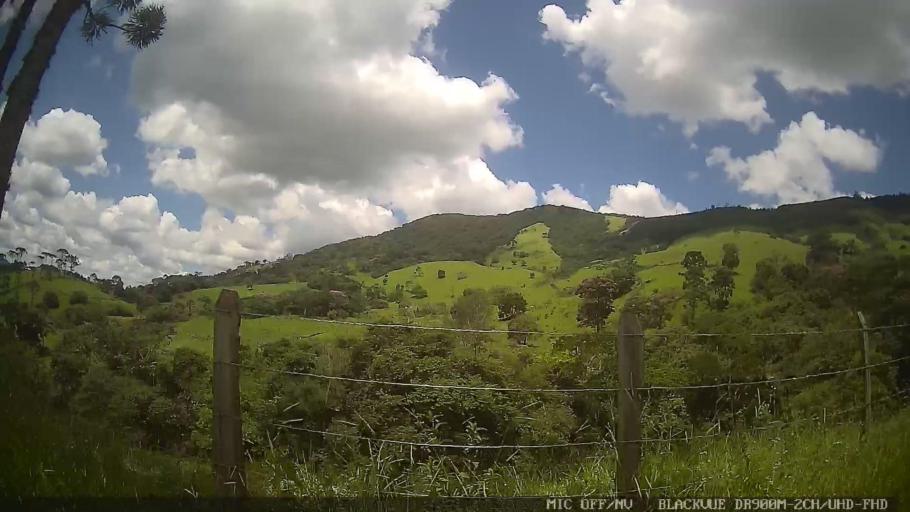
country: BR
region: Minas Gerais
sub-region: Extrema
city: Extrema
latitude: -22.8714
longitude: -46.2903
